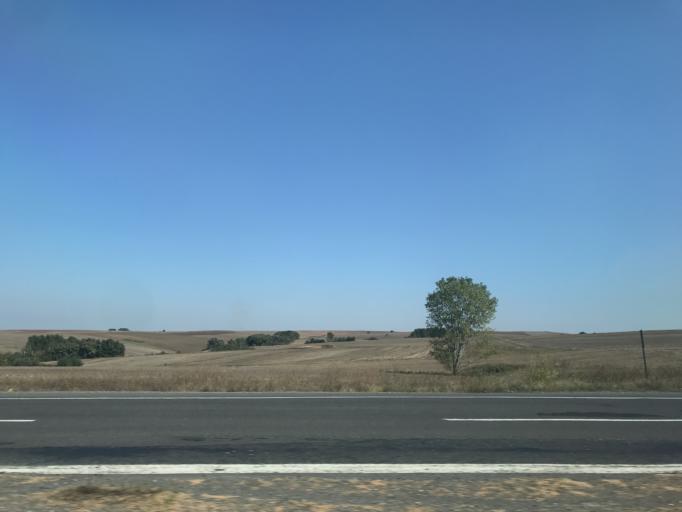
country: TR
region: Tekirdag
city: Muratli
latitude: 41.1153
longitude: 27.4909
